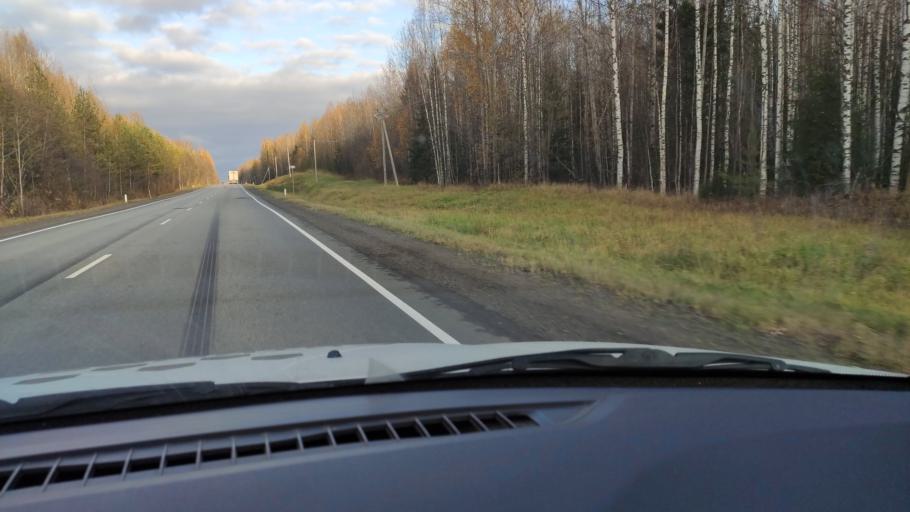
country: RU
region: Kirov
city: Belaya Kholunitsa
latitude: 58.9152
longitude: 51.0857
